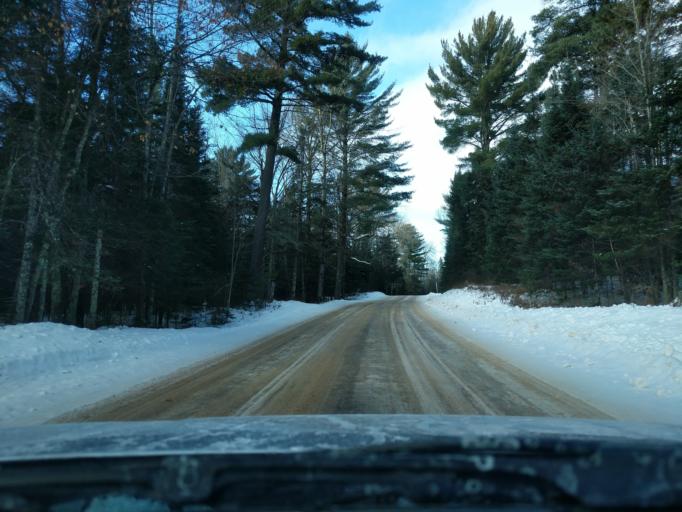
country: US
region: Wisconsin
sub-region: Vilas County
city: Eagle River
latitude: 45.8036
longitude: -89.0701
